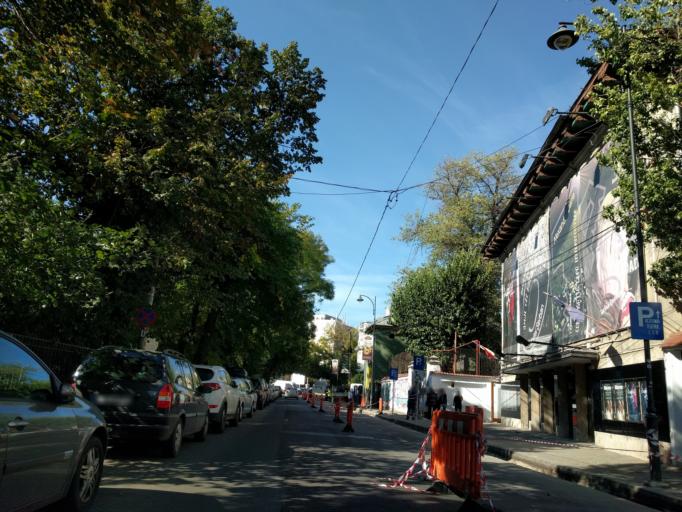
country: RO
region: Bucuresti
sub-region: Municipiul Bucuresti
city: Bucharest
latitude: 44.4434
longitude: 26.1045
